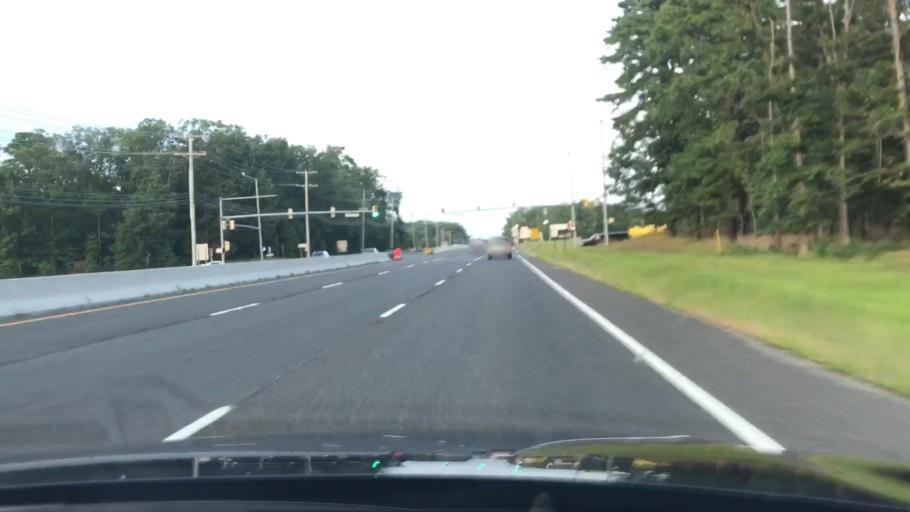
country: US
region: New Jersey
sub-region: Monmouth County
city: Shrewsbury
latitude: 40.1503
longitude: -74.4382
